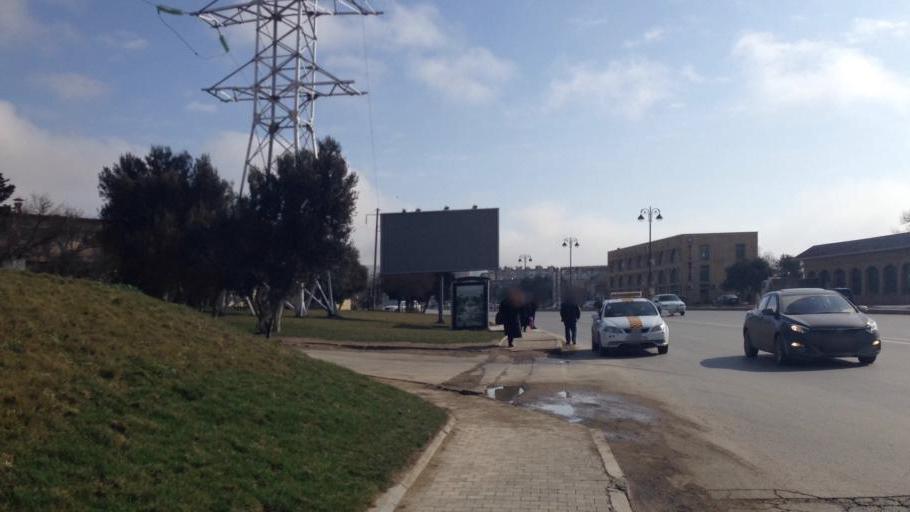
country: AZ
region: Baki
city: Baku
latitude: 40.3704
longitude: 49.9317
